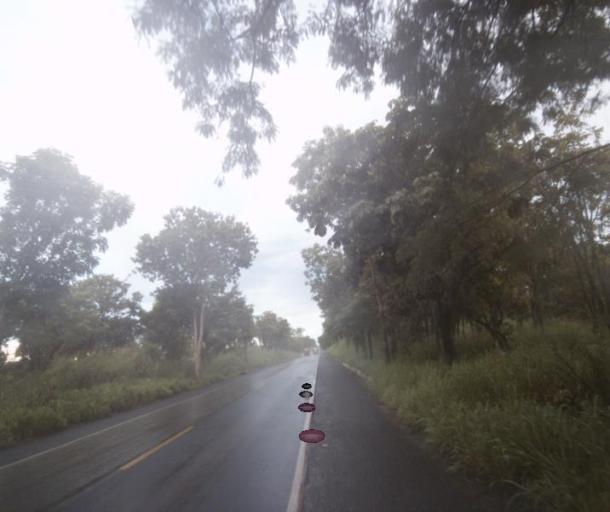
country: BR
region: Goias
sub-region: Porangatu
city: Porangatu
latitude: -13.8023
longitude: -49.0373
